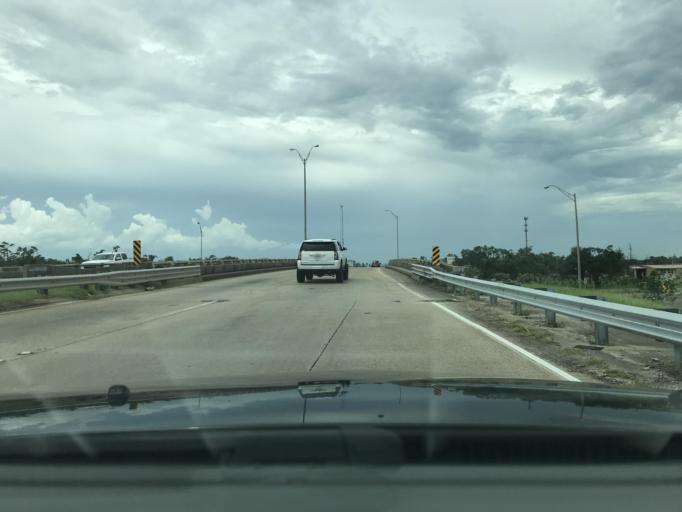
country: US
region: Louisiana
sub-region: Calcasieu Parish
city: Lake Charles
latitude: 30.2459
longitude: -93.1803
